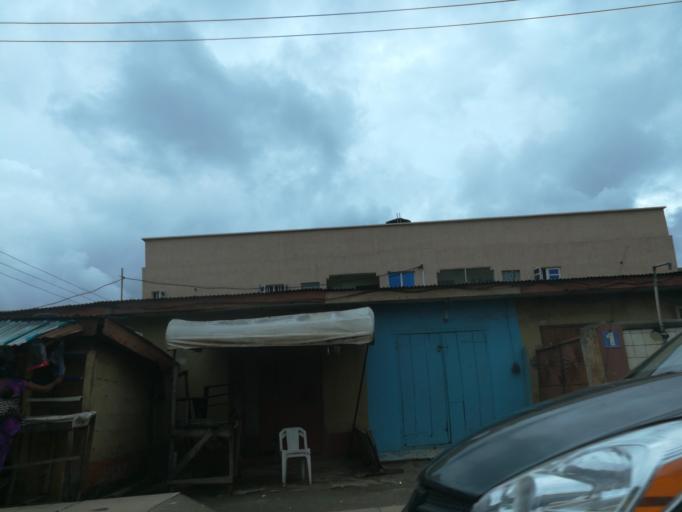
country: NG
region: Lagos
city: Agege
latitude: 6.6151
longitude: 3.3117
